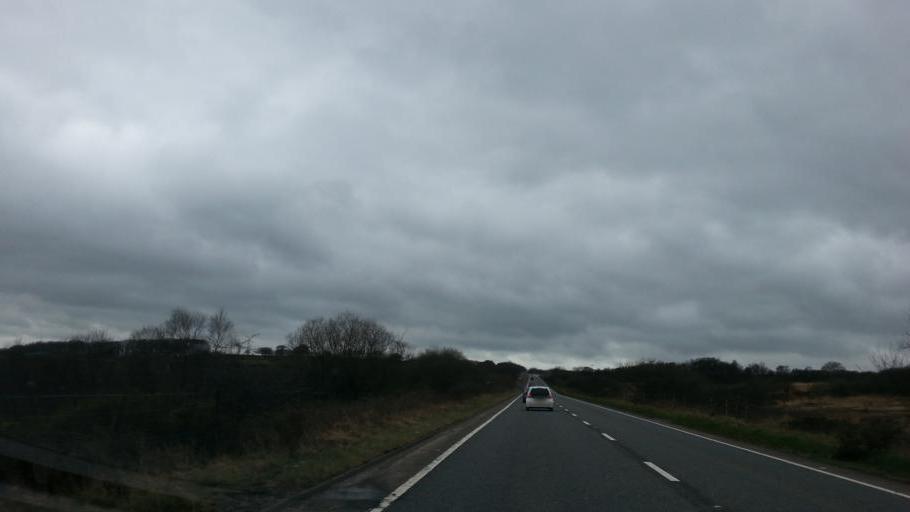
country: GB
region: England
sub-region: Devon
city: South Molton
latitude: 50.9814
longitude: -3.6551
